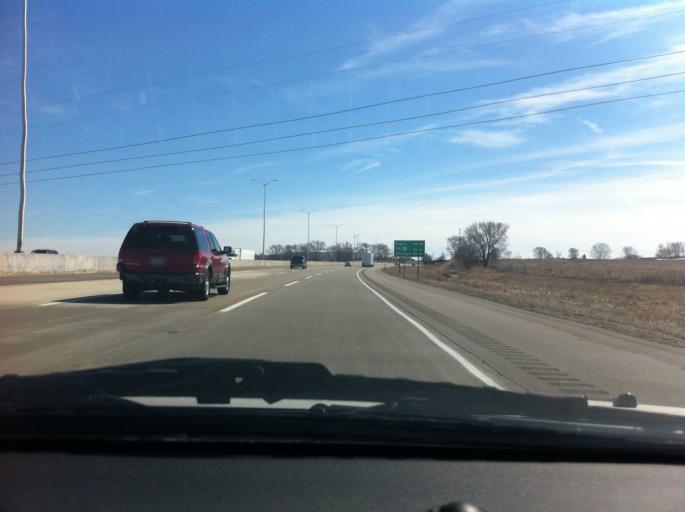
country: US
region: Illinois
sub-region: Winnebago County
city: Cherry Valley
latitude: 42.2906
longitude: -88.9650
